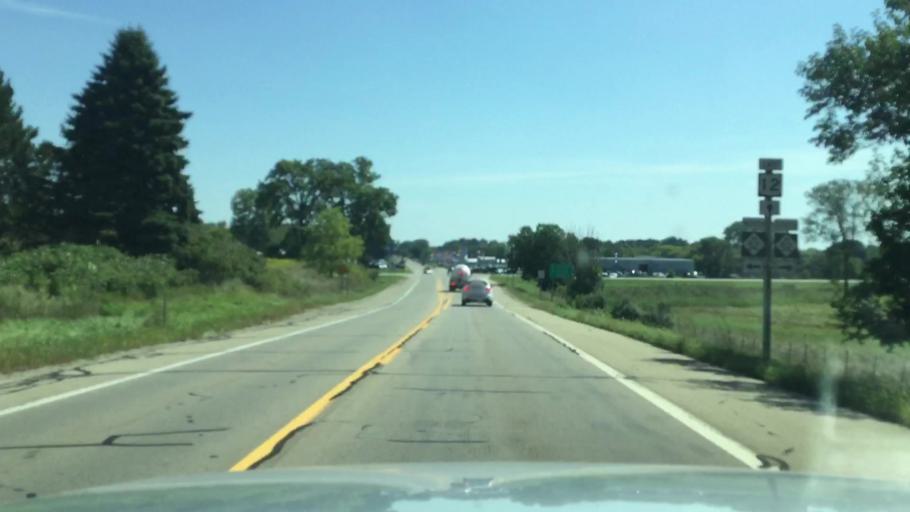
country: US
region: Michigan
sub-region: Lenawee County
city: Clinton
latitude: 42.0719
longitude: -84.0164
